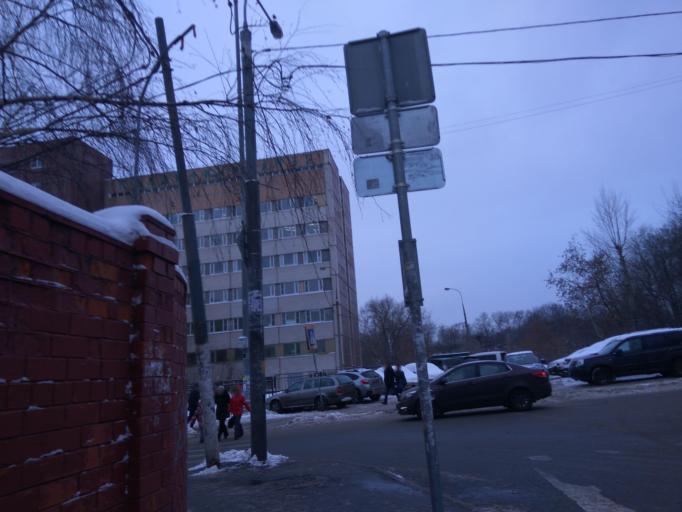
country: RU
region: Moscow
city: Tsaritsyno
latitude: 55.6190
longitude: 37.6660
